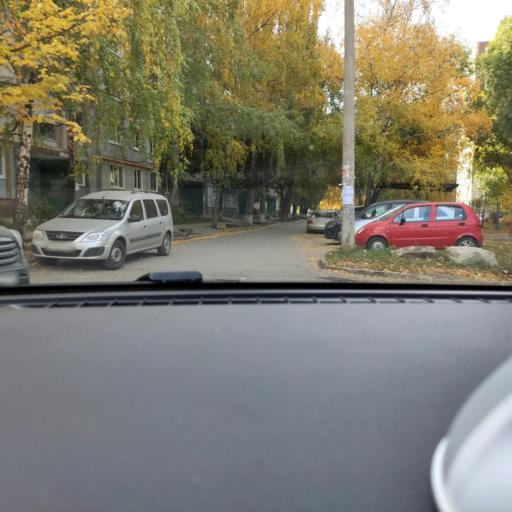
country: RU
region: Samara
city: Samara
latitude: 53.2654
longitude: 50.2230
